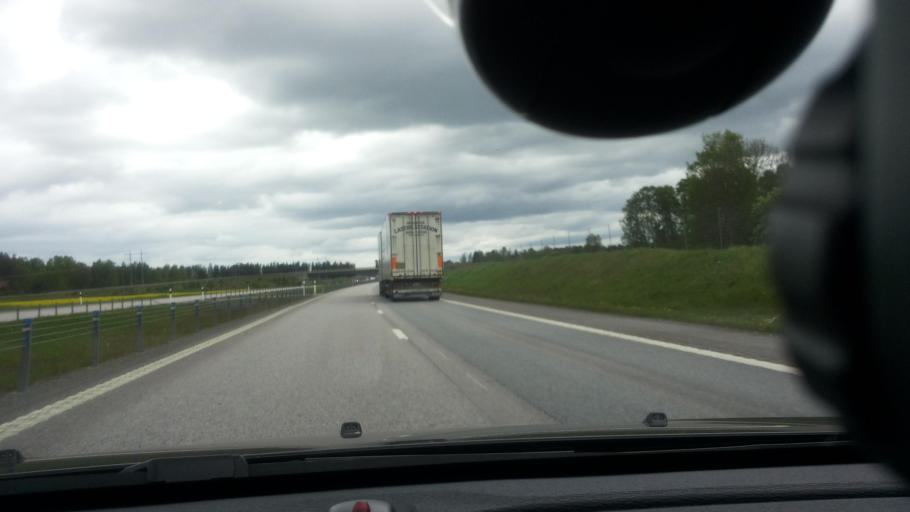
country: SE
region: Uppsala
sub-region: Osthammars Kommun
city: Bjorklinge
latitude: 60.0986
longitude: 17.5669
